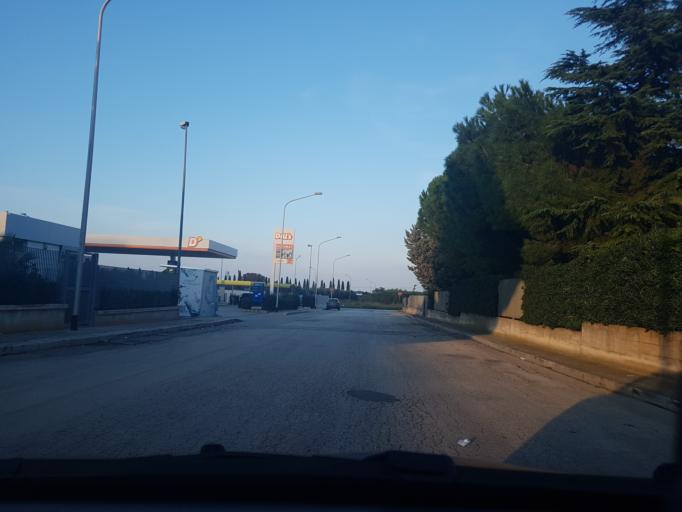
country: IT
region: Apulia
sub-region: Provincia di Bari
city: Bitritto
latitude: 41.0462
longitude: 16.8310
